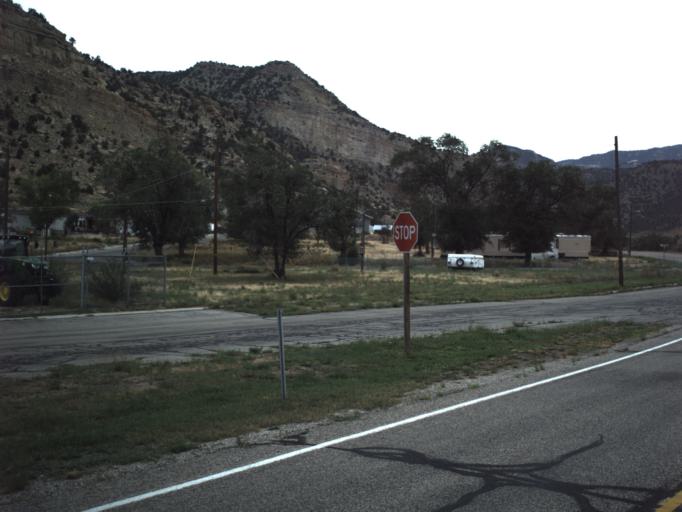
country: US
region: Utah
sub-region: Carbon County
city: East Carbon City
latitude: 39.5513
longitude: -110.3852
